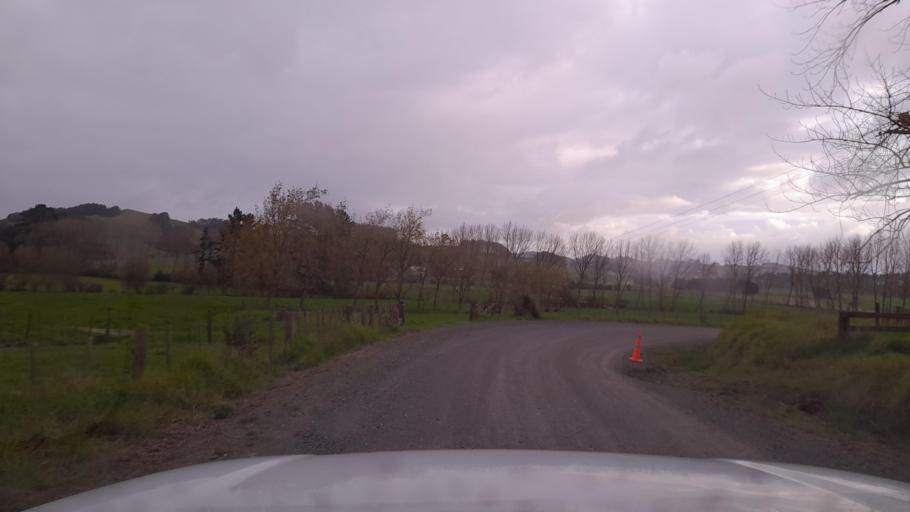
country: NZ
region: Northland
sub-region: Whangarei
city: Maungatapere
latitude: -35.6311
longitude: 174.1946
